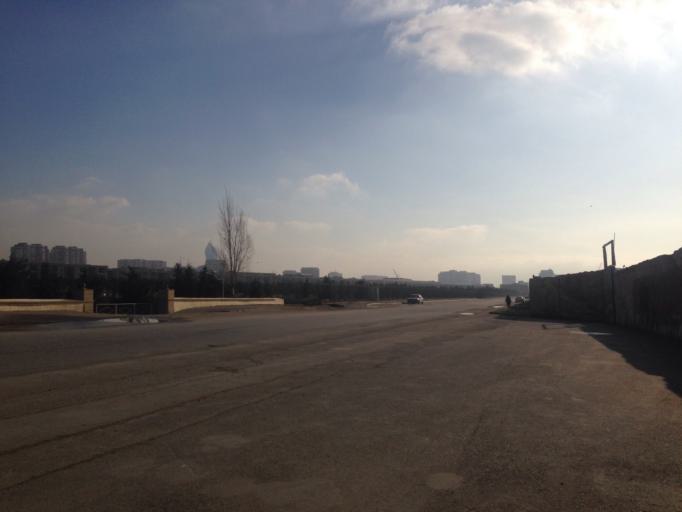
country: AZ
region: Baki
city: Baku
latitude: 40.4110
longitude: 49.8537
